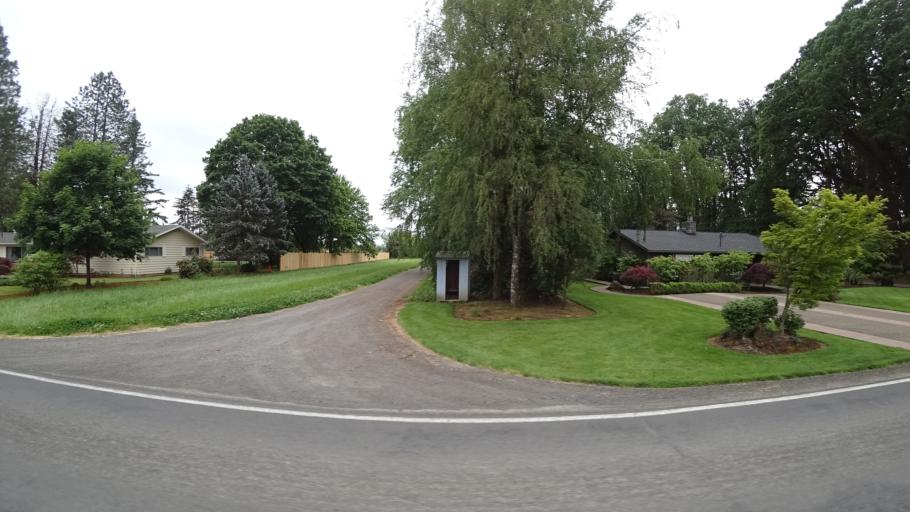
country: US
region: Oregon
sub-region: Washington County
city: Hillsboro
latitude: 45.4802
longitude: -122.9889
